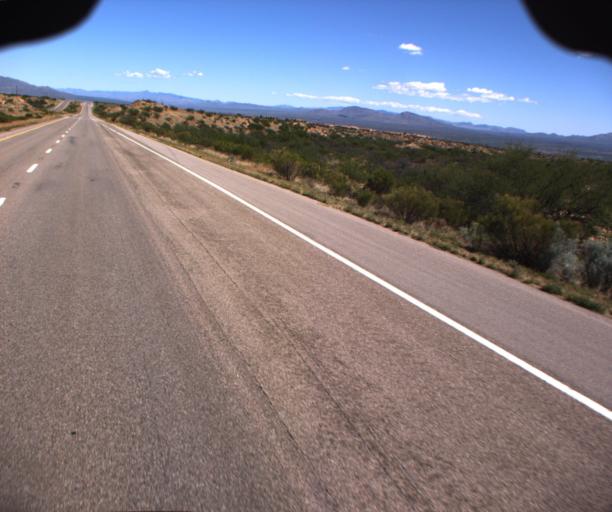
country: US
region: Arizona
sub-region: Cochise County
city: Whetstone
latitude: 31.9307
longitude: -110.3410
